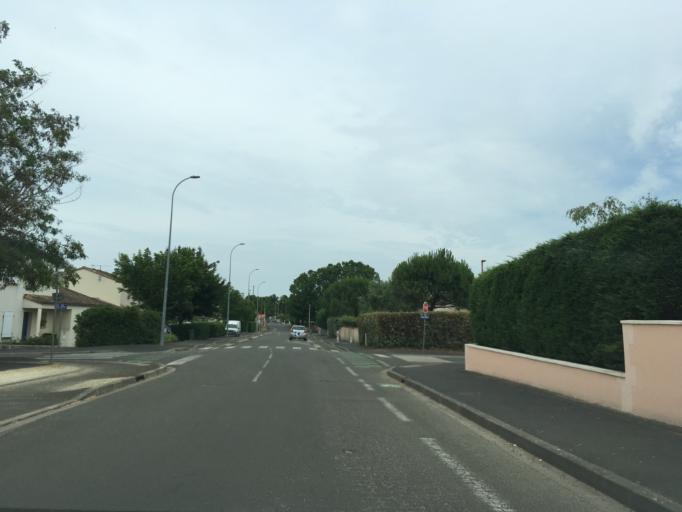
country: FR
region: Poitou-Charentes
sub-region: Departement des Deux-Sevres
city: Bessines
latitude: 46.3203
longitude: -0.5143
